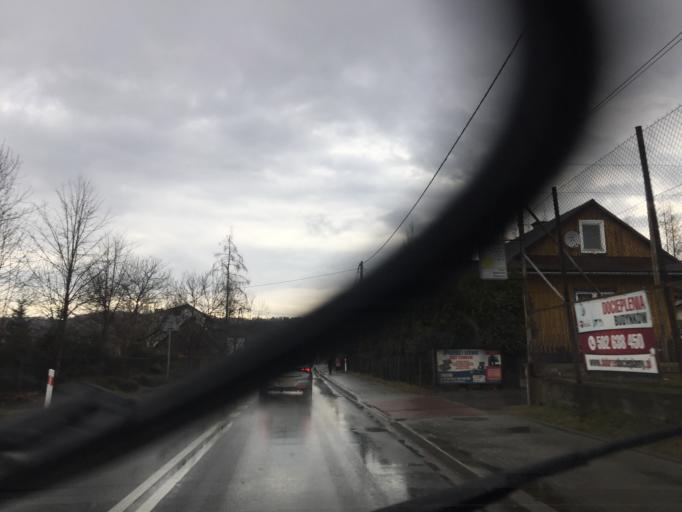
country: PL
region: Lesser Poland Voivodeship
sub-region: Powiat wadowicki
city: Izdebnik
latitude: 49.8732
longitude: 19.7922
